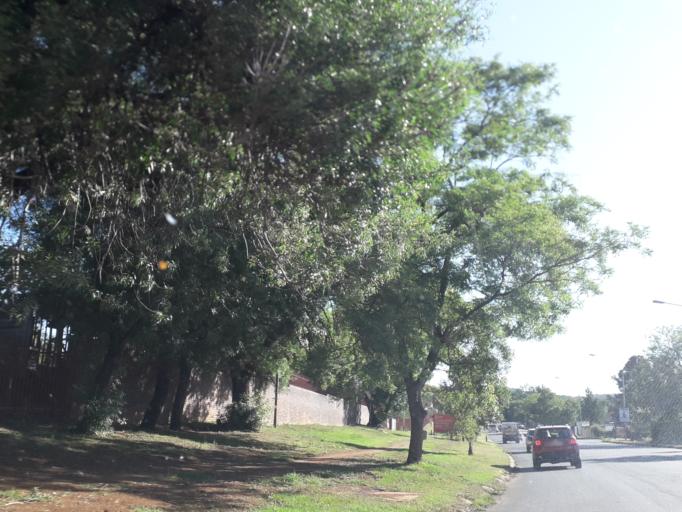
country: ZA
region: Gauteng
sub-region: City of Johannesburg Metropolitan Municipality
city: Roodepoort
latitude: -26.1378
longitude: 27.9595
